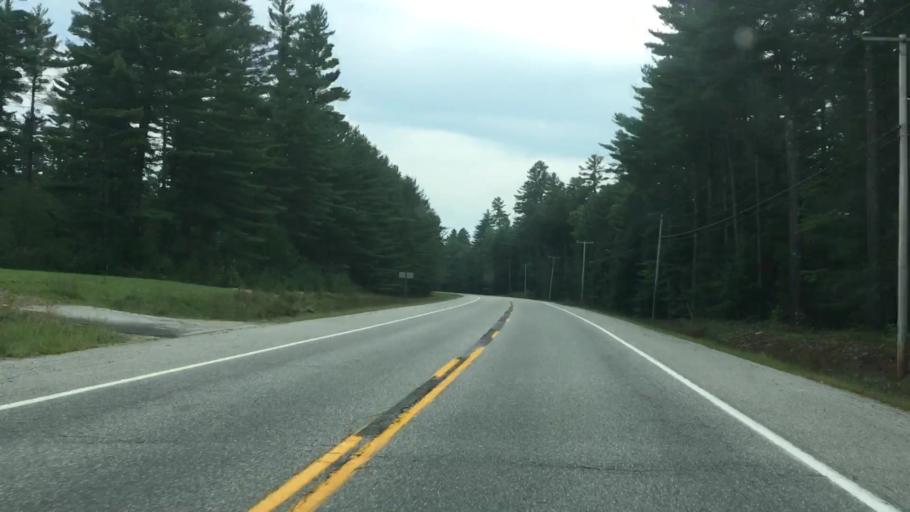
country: US
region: Maine
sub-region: Oxford County
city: Bethel
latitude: 44.4635
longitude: -70.8029
